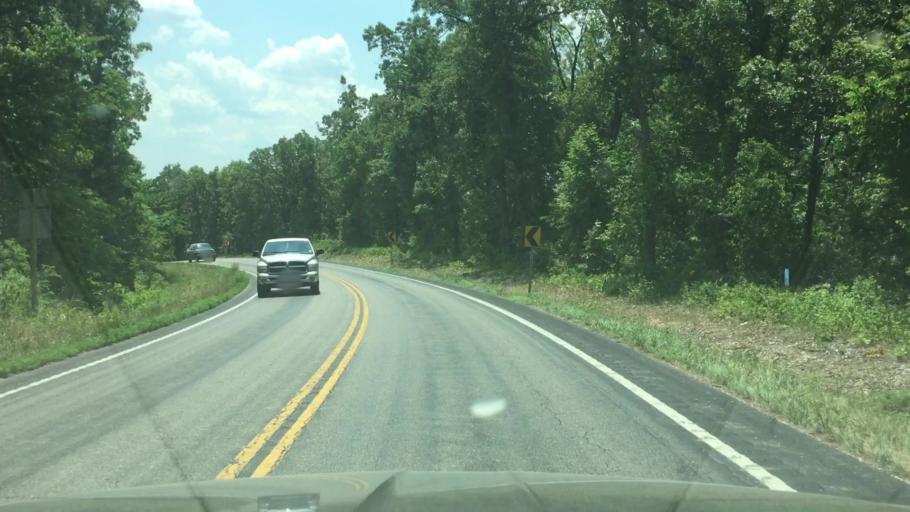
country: US
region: Missouri
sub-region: Camden County
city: Osage Beach
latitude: 38.1270
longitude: -92.5577
